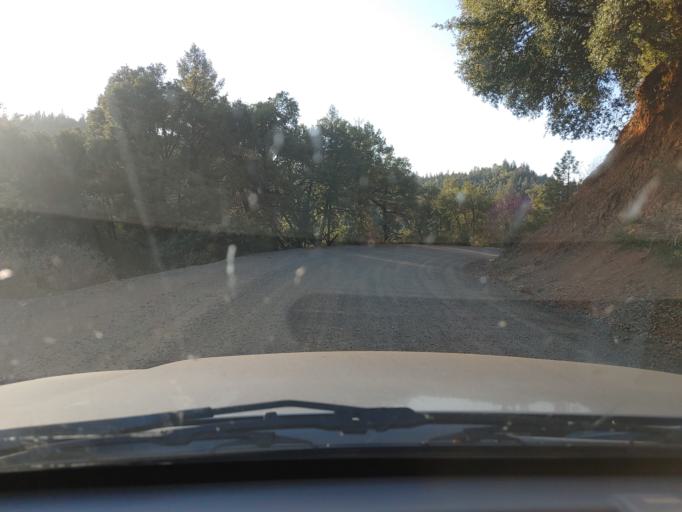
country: US
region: California
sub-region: Shasta County
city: Bella Vista
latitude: 40.8323
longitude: -122.0181
